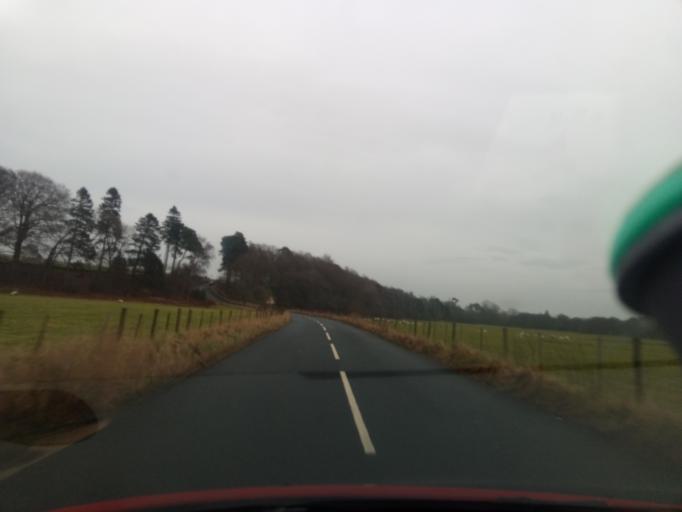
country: GB
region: England
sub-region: Northumberland
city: Birtley
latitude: 55.1485
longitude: -2.2788
